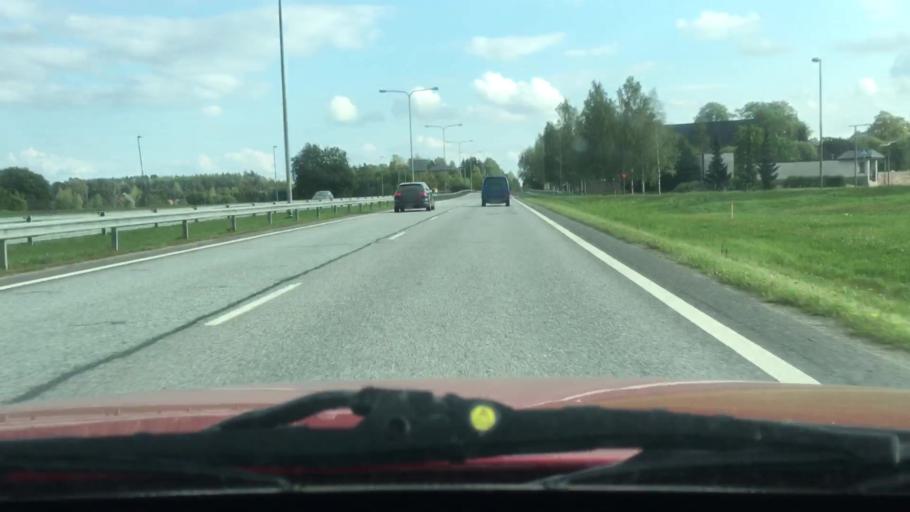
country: FI
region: Varsinais-Suomi
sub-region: Turku
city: Raisio
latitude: 60.4872
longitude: 22.1757
